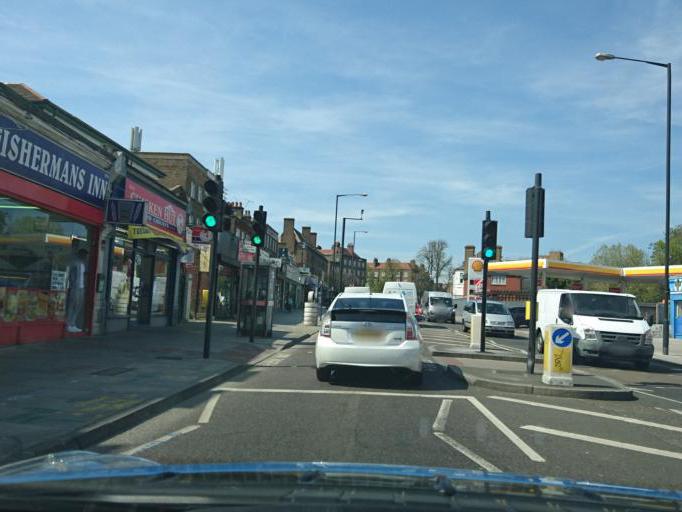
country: GB
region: England
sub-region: Greater London
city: Hackney
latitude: 51.5636
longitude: -0.0589
